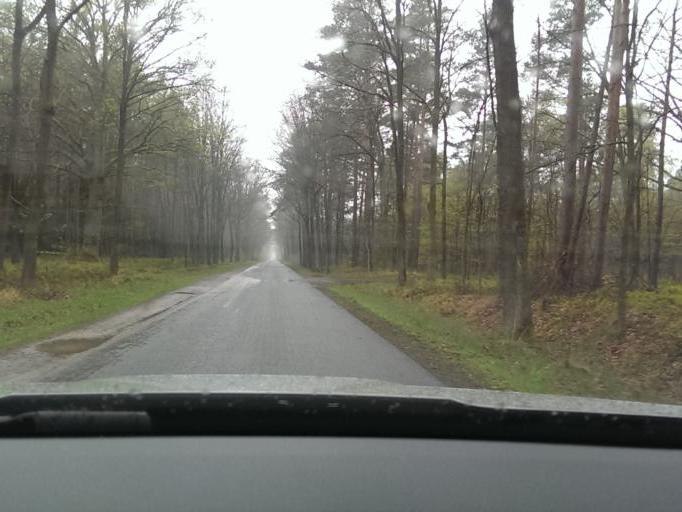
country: DE
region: Lower Saxony
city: Elze
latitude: 52.6075
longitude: 9.7750
